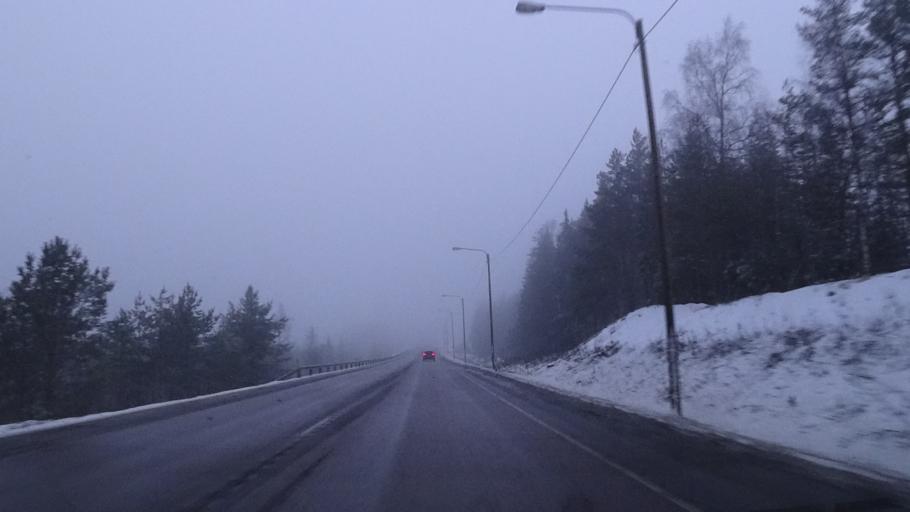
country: FI
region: Paijanne Tavastia
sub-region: Lahti
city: Hollola
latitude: 60.9869
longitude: 25.4003
